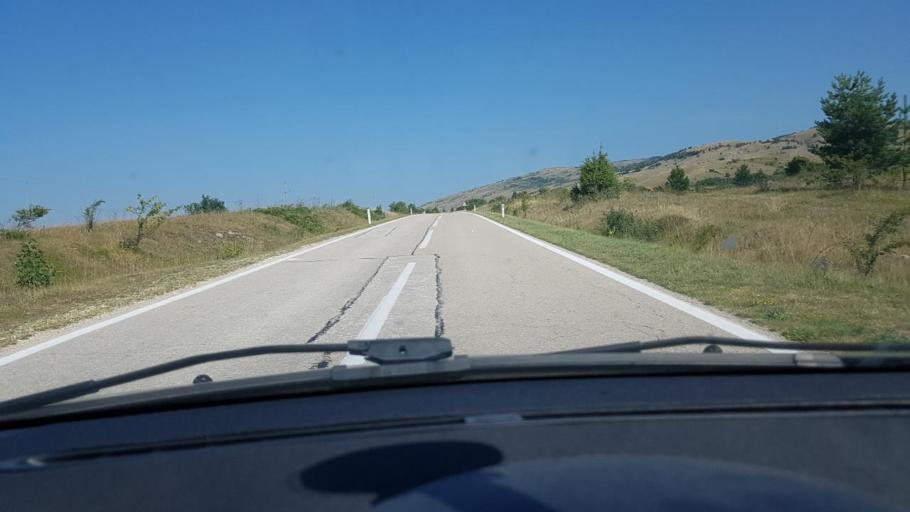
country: BA
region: Federation of Bosnia and Herzegovina
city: Bosansko Grahovo
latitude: 44.1136
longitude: 16.5400
